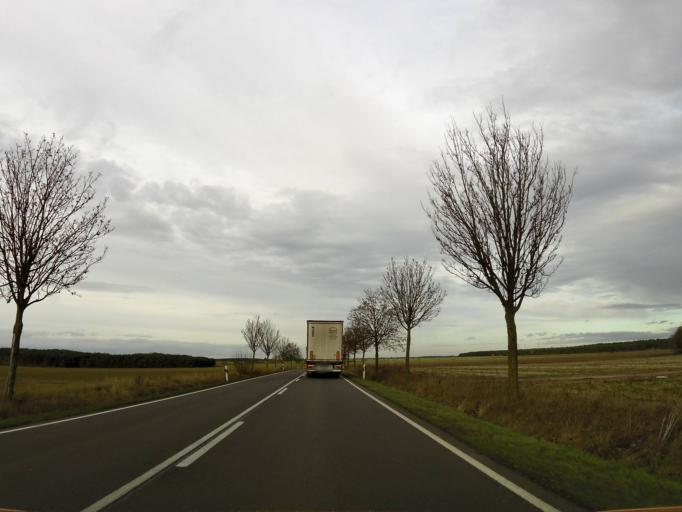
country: DE
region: Saxony-Anhalt
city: Pretzier
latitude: 52.7119
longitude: 11.2509
